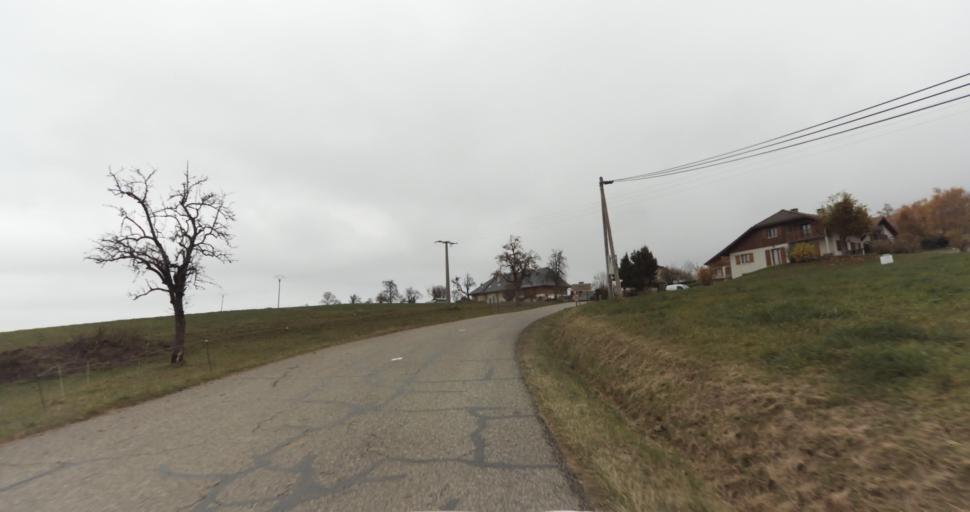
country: FR
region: Rhone-Alpes
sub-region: Departement de la Haute-Savoie
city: Saint-Jorioz
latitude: 45.8031
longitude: 6.1584
